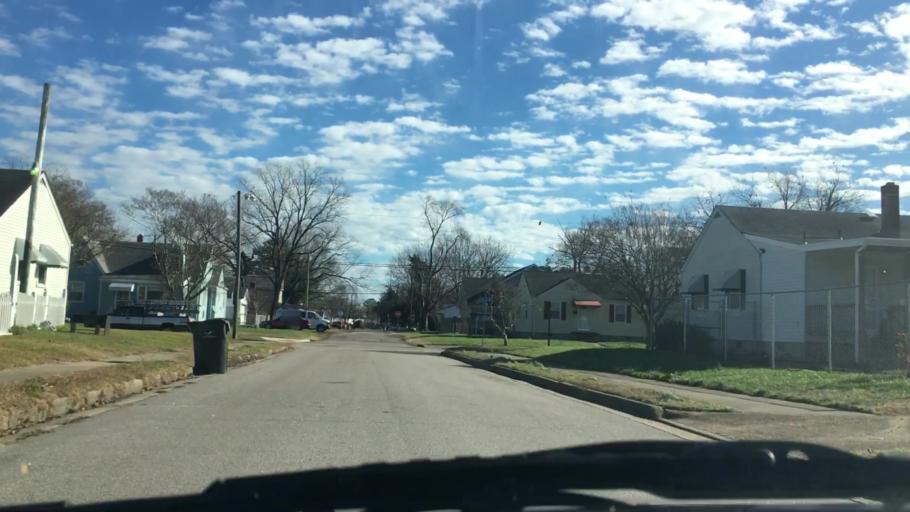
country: US
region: Virginia
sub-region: City of Norfolk
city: Norfolk
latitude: 36.8801
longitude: -76.2576
